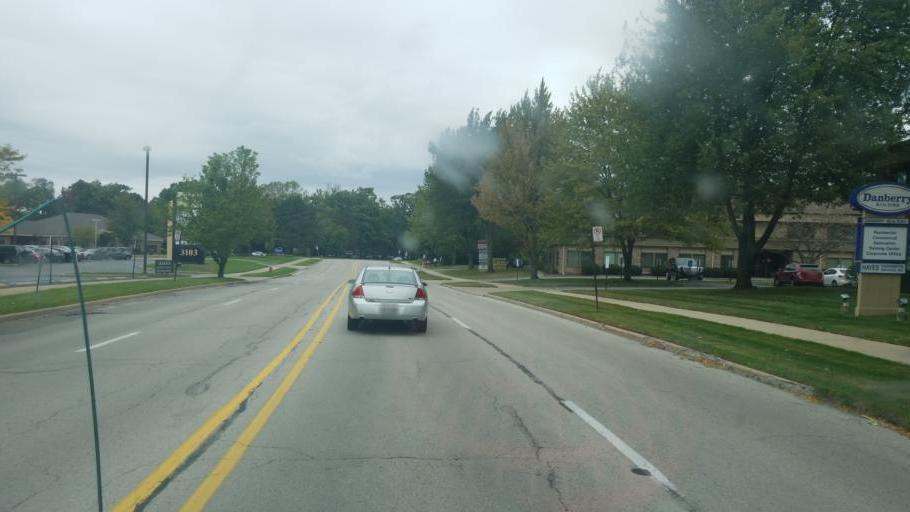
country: US
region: Ohio
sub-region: Lucas County
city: Ottawa Hills
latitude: 41.6797
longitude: -83.6285
